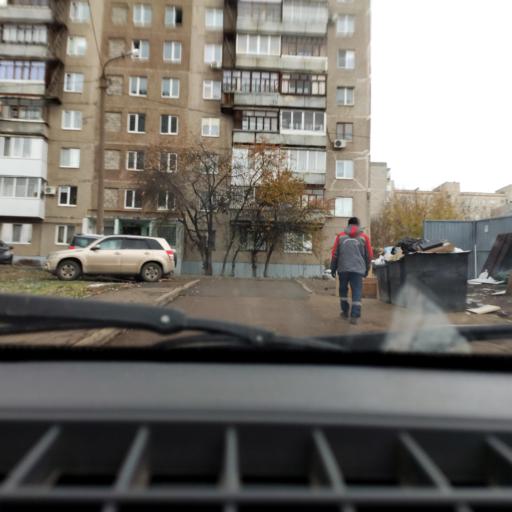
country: RU
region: Bashkortostan
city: Ufa
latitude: 54.7779
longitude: 56.0395
